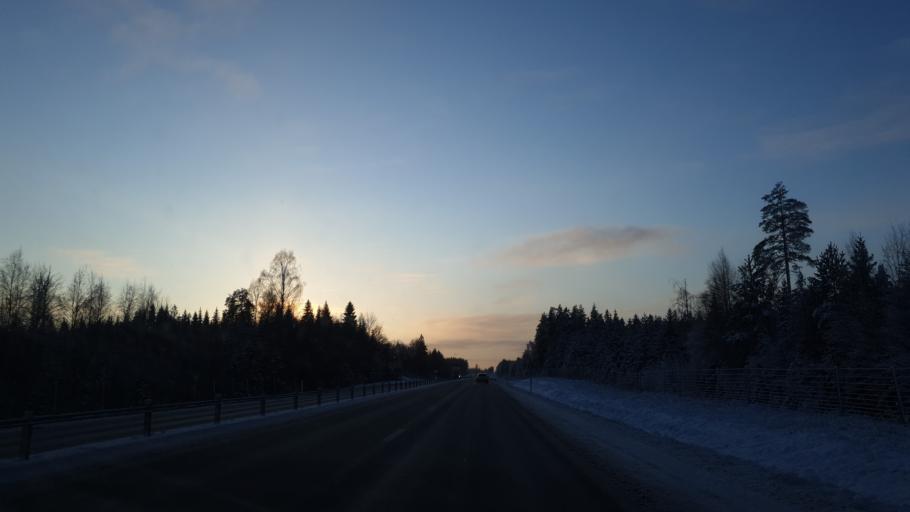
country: SE
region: Vaesterbotten
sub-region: Umea Kommun
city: Hoernefors
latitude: 63.6617
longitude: 19.9628
